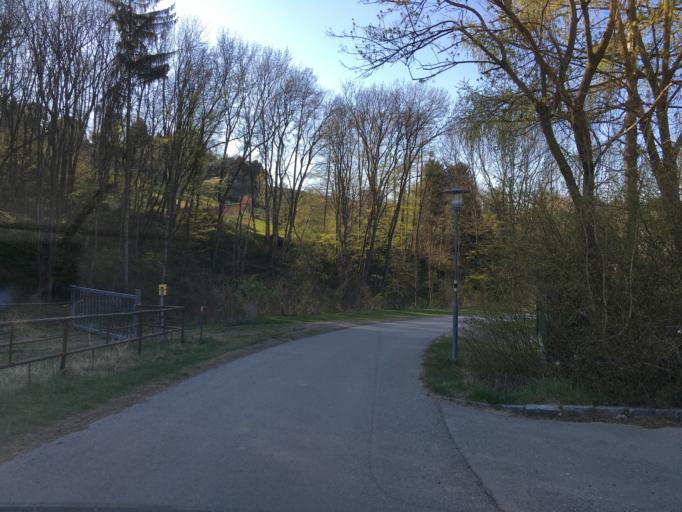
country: AT
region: Lower Austria
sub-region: Politischer Bezirk Tulln
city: Konigstetten
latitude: 48.2949
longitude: 16.1542
